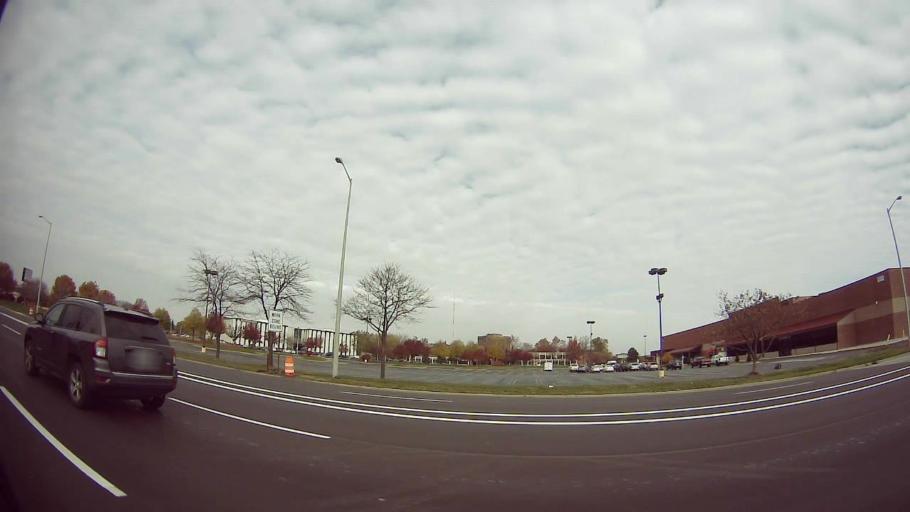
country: US
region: Michigan
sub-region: Oakland County
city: Oak Park
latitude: 42.4447
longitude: -83.2089
